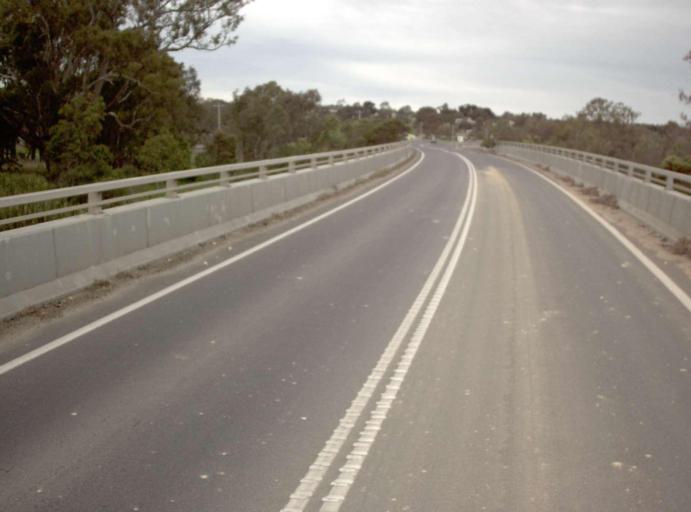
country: AU
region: Victoria
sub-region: Wellington
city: Sale
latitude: -38.1510
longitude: 147.0814
